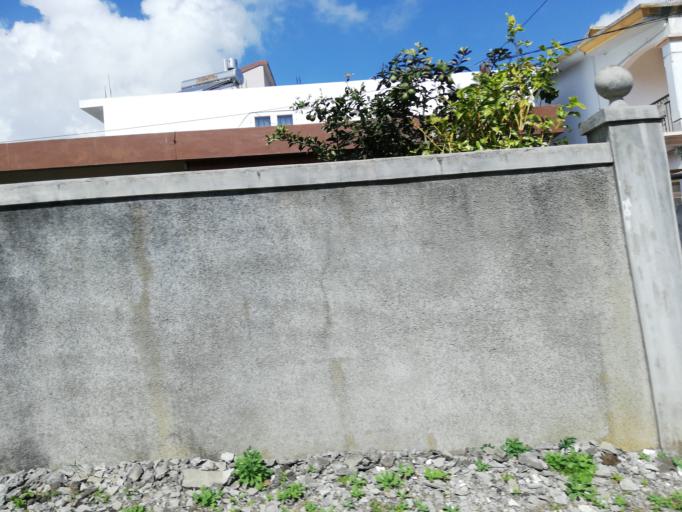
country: MU
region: Moka
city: Verdun
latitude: -20.2197
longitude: 57.5379
